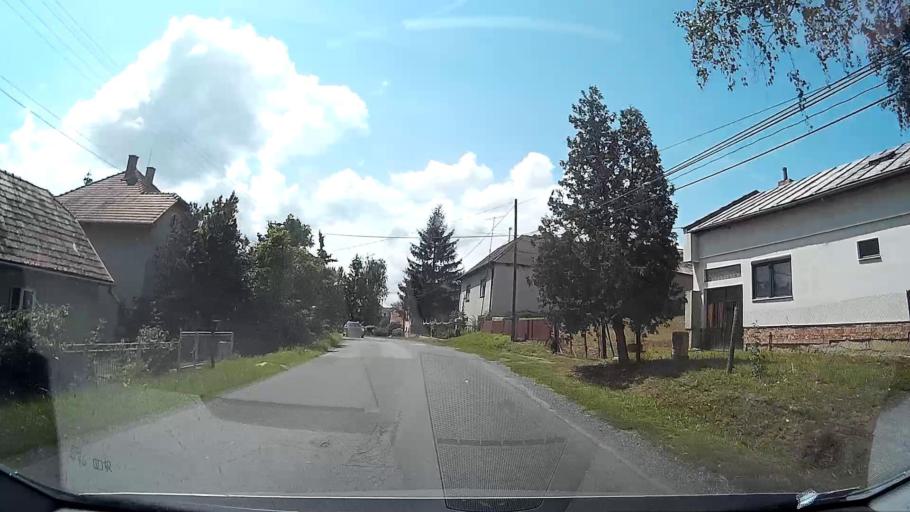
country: SK
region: Banskobystricky
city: Fil'akovo
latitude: 48.3017
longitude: 19.7924
